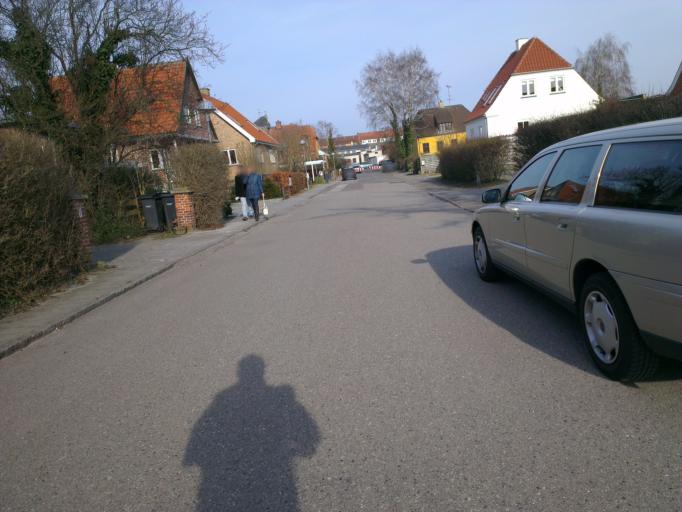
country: DK
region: Capital Region
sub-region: Frederikssund Kommune
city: Frederikssund
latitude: 55.8368
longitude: 12.0617
